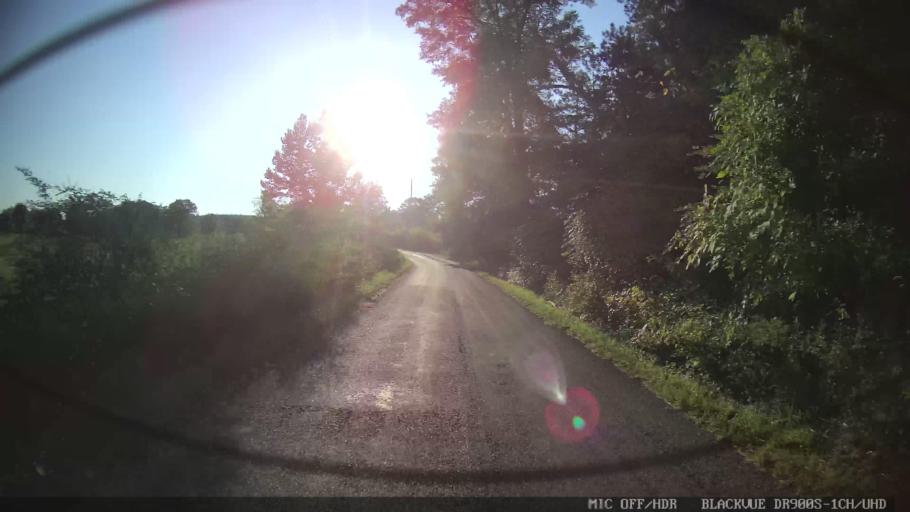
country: US
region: Tennessee
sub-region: Bradley County
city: Wildwood Lake
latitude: 35.0145
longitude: -84.7413
